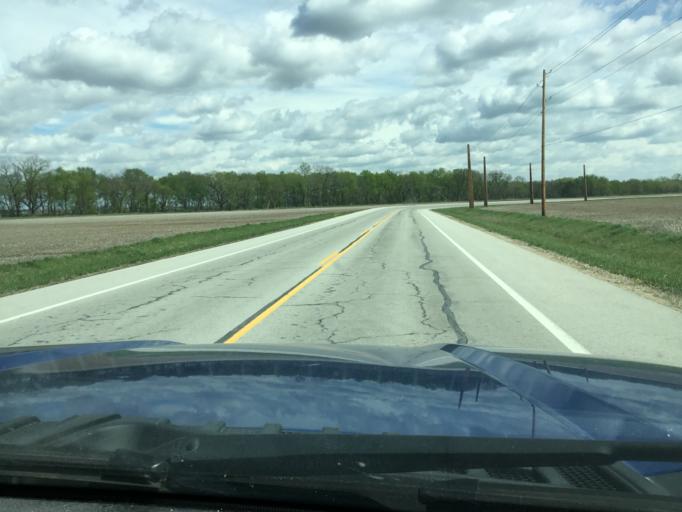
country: US
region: Kansas
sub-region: Douglas County
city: Lawrence
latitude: 38.9136
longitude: -95.2698
